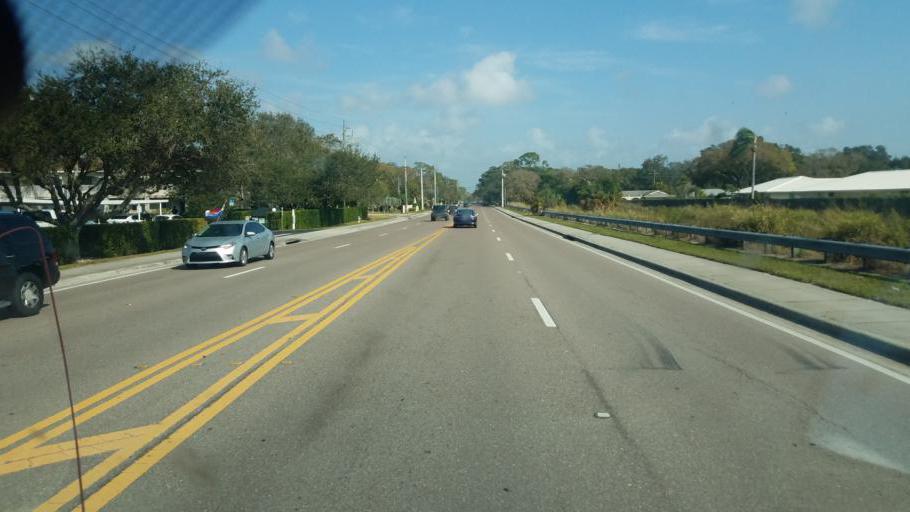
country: US
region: Florida
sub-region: Sarasota County
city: Southgate
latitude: 27.3083
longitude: -82.4956
